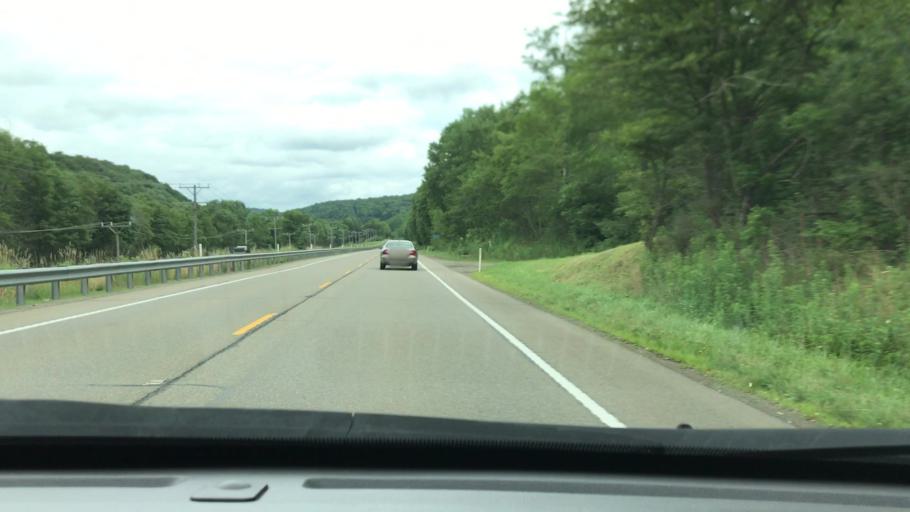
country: US
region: Pennsylvania
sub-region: Elk County
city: Johnsonburg
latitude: 41.5465
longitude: -78.6819
